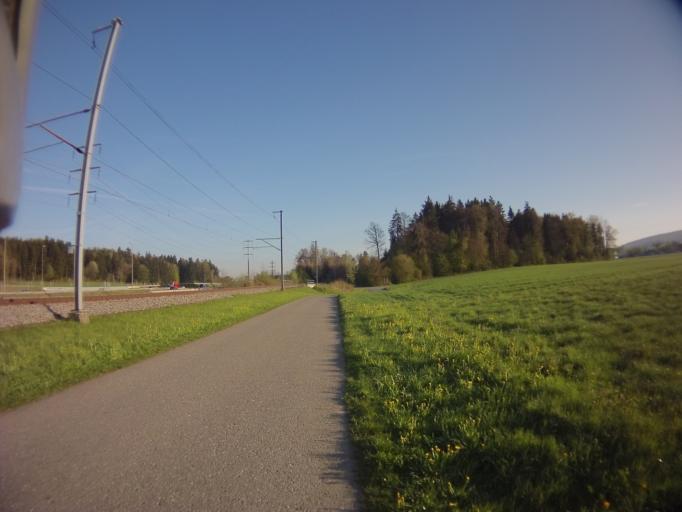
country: CH
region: Zurich
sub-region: Bezirk Affoltern
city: Obfelden / Toussen
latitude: 47.2654
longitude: 8.4410
